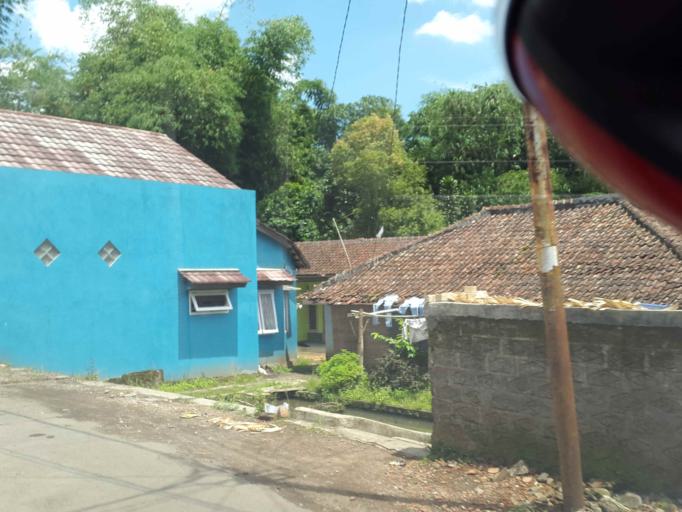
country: ID
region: West Java
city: Sukabumi
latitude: -6.9054
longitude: 106.9440
